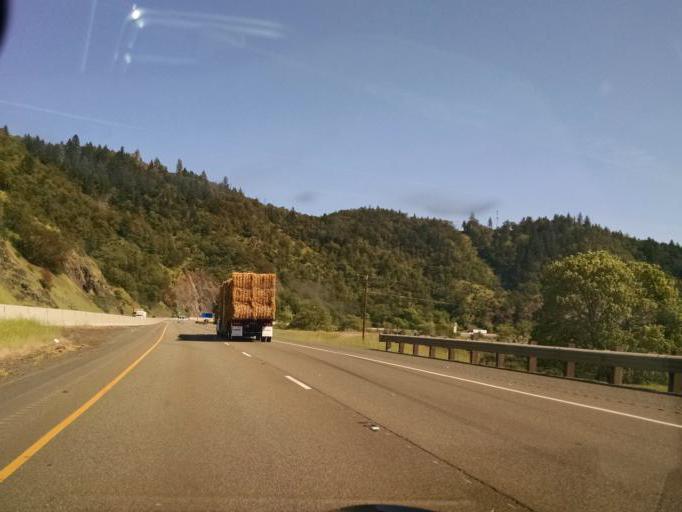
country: US
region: Oregon
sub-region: Douglas County
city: Tri-City
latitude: 42.9633
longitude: -123.3312
